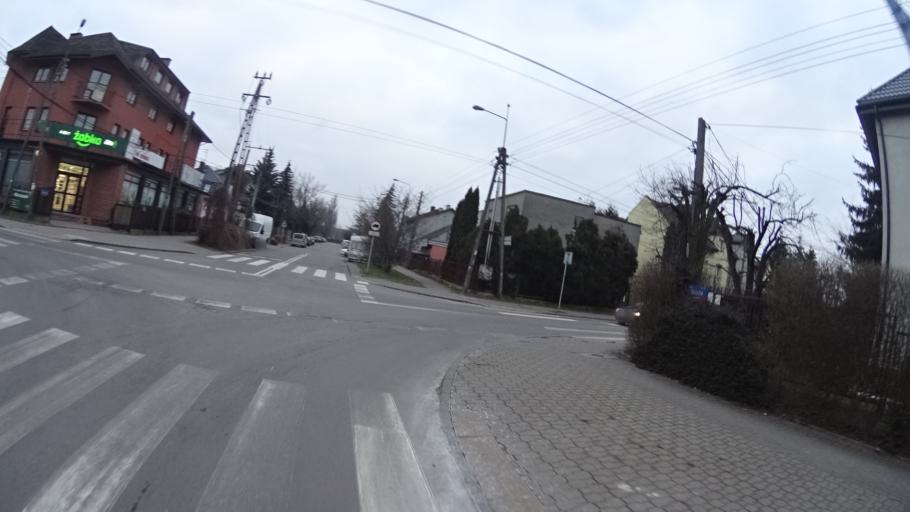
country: PL
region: Masovian Voivodeship
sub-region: Warszawa
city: Bemowo
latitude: 52.2322
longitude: 20.9248
